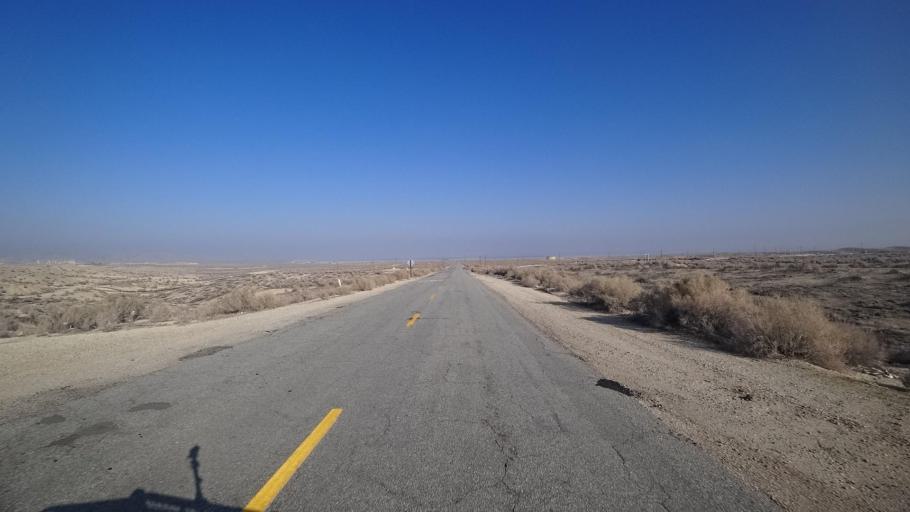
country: US
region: California
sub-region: Kern County
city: Maricopa
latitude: 35.0966
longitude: -119.4100
